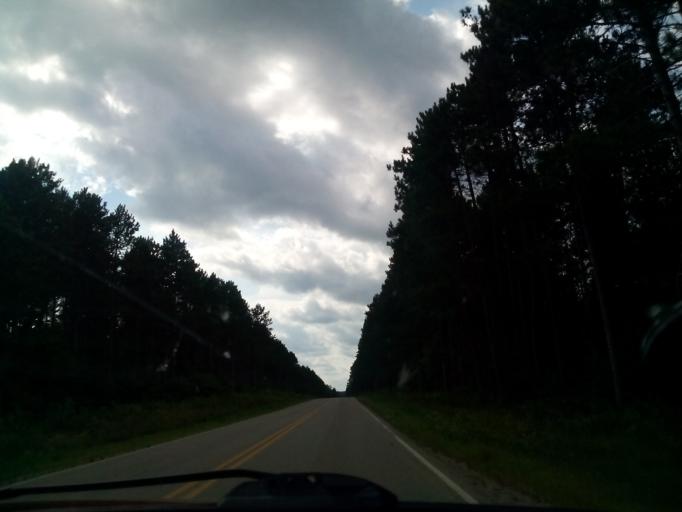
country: US
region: Michigan
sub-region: Dickinson County
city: Kingsford
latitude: 45.4020
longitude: -88.2227
